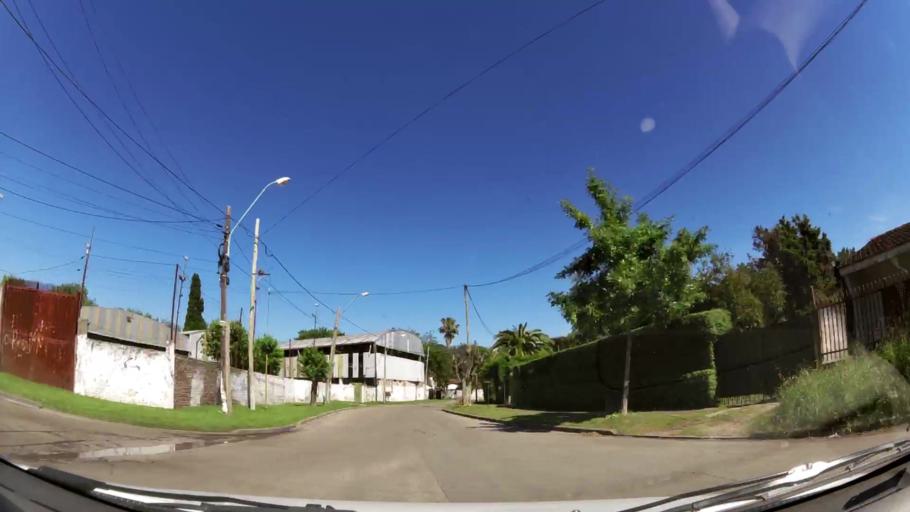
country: AR
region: Buenos Aires
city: Ituzaingo
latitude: -34.6235
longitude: -58.6582
